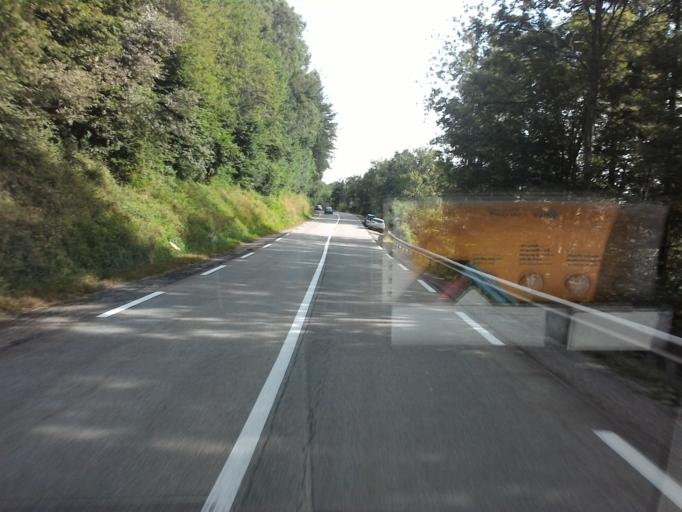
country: FR
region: Rhone-Alpes
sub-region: Departement de l'Isere
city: Notre-Dame-de-Mesage
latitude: 45.0141
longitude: 5.7742
